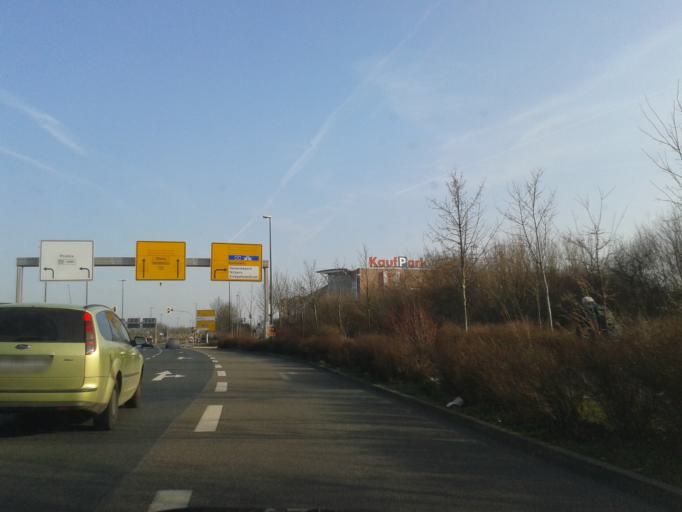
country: DE
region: Saxony
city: Kreischa
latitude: 50.9993
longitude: 13.7980
